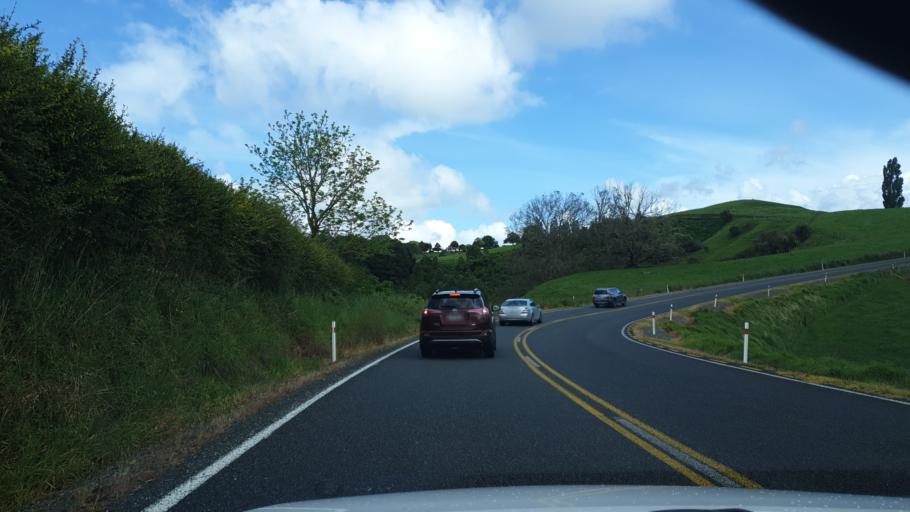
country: NZ
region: Waikato
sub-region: Matamata-Piako District
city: Matamata
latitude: -37.8809
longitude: 175.6939
